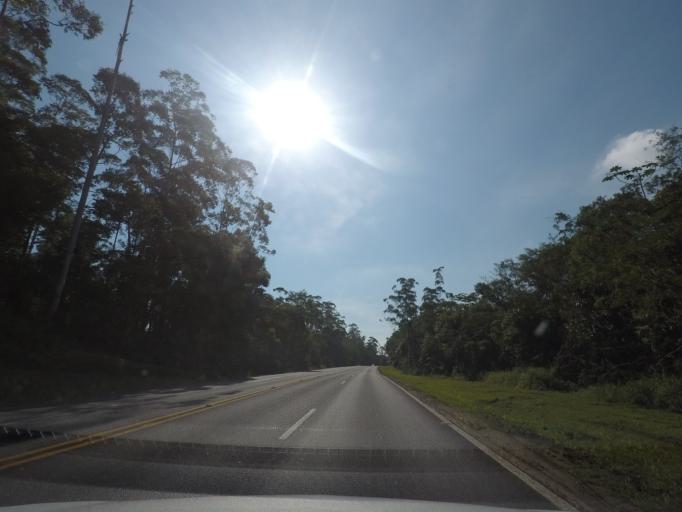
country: BR
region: Parana
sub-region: Pontal Do Parana
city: Pontal do Parana
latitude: -25.6032
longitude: -48.6087
